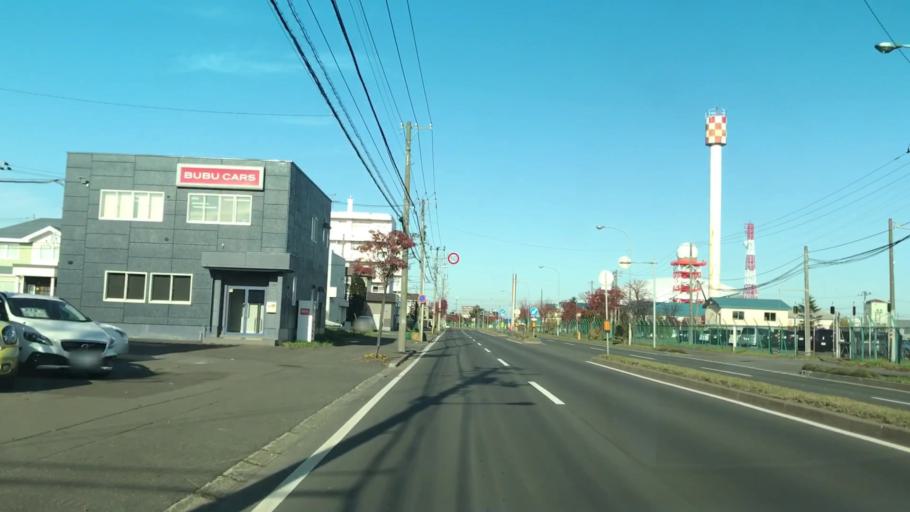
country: JP
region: Hokkaido
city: Sapporo
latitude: 43.1108
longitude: 141.3793
